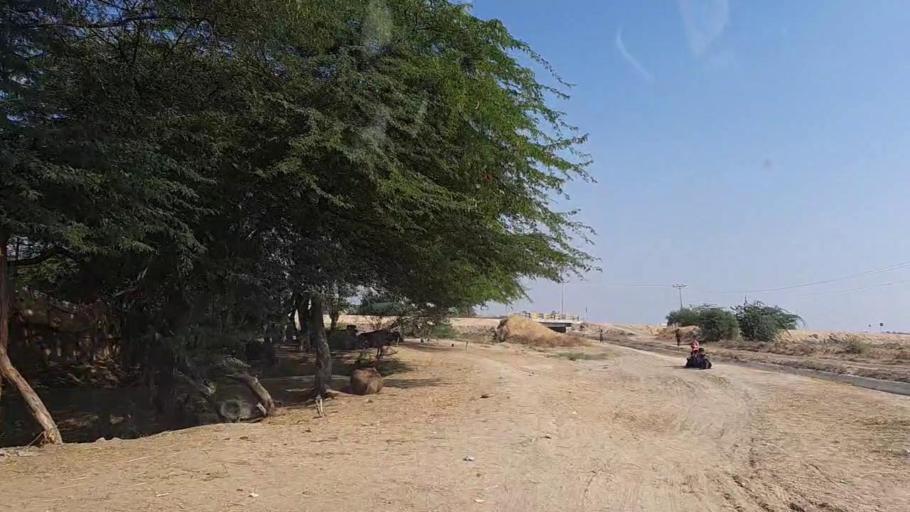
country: PK
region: Sindh
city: Thatta
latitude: 24.7624
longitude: 67.9479
